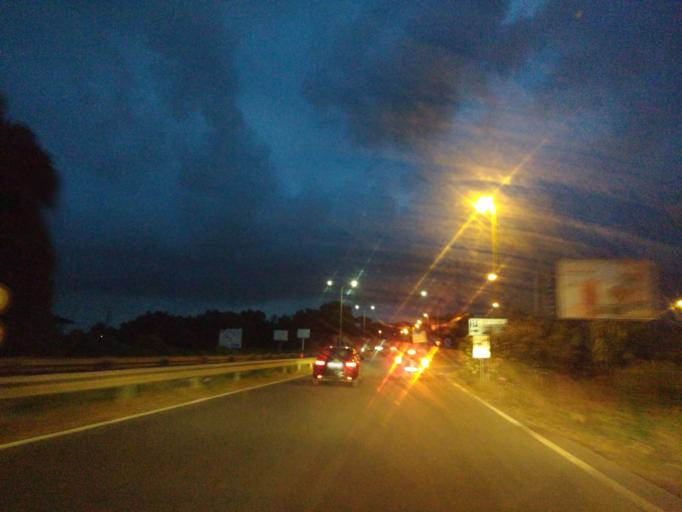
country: IT
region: Latium
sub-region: Citta metropolitana di Roma Capitale
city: Anzio
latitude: 41.4614
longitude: 12.6216
